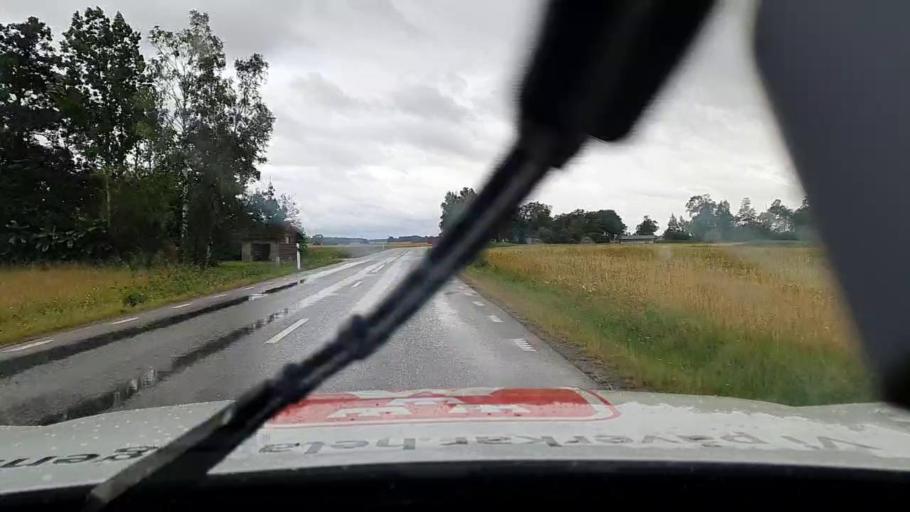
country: SE
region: Vaestra Goetaland
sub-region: Toreboda Kommun
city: Toereboda
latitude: 58.6225
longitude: 14.0138
